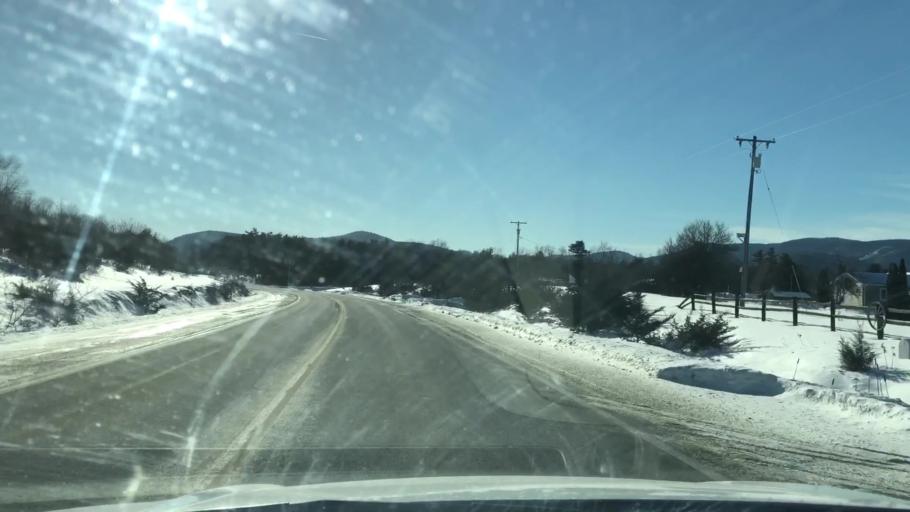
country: US
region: New York
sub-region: Essex County
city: Ticonderoga
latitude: 43.8651
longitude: -73.4086
